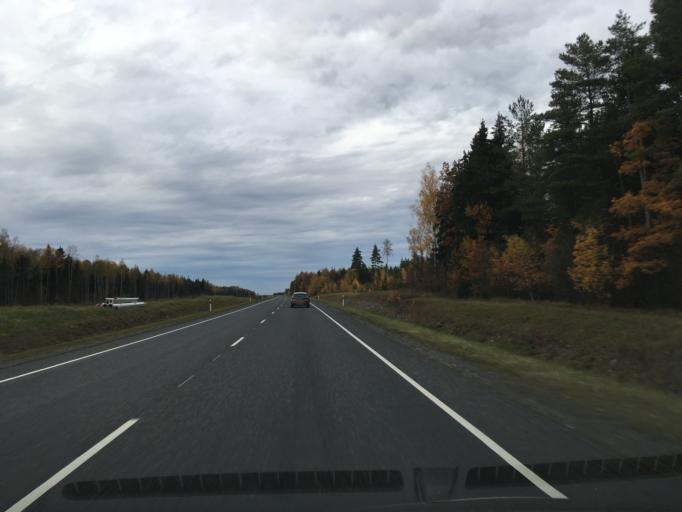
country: EE
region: Harju
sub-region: Nissi vald
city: Turba
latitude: 58.9517
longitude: 24.0814
